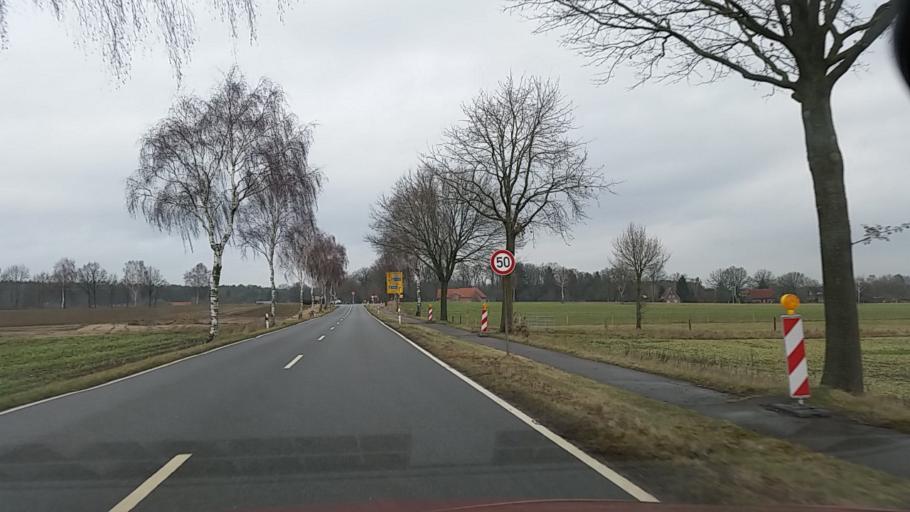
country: DE
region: Lower Saxony
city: Bispingen
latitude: 53.1246
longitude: 9.9997
